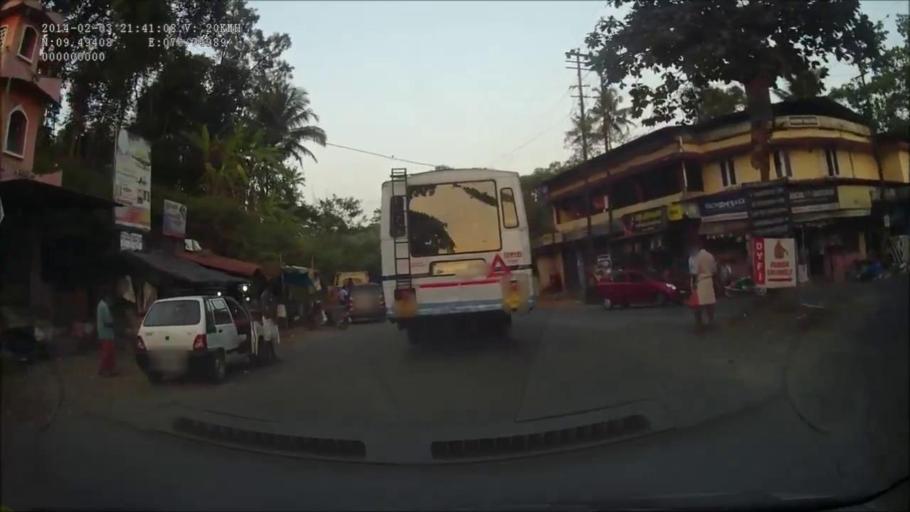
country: IN
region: Kerala
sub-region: Kottayam
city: Erattupetta
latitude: 9.4950
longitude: 76.7510
